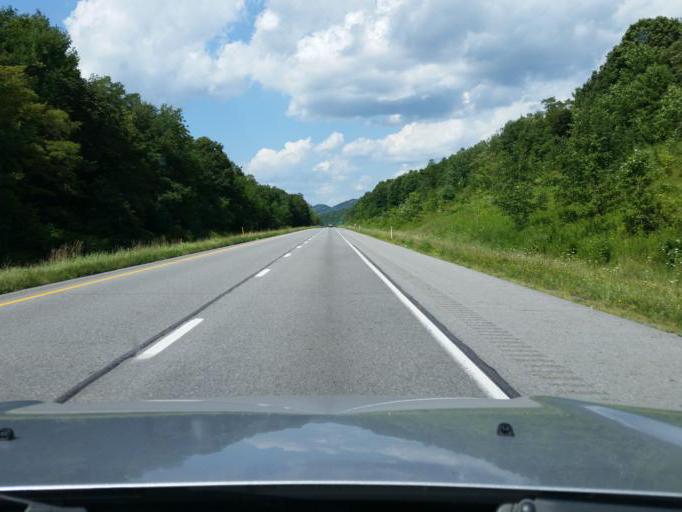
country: US
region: Pennsylvania
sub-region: Blair County
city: Claysburg
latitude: 40.2203
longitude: -78.4706
